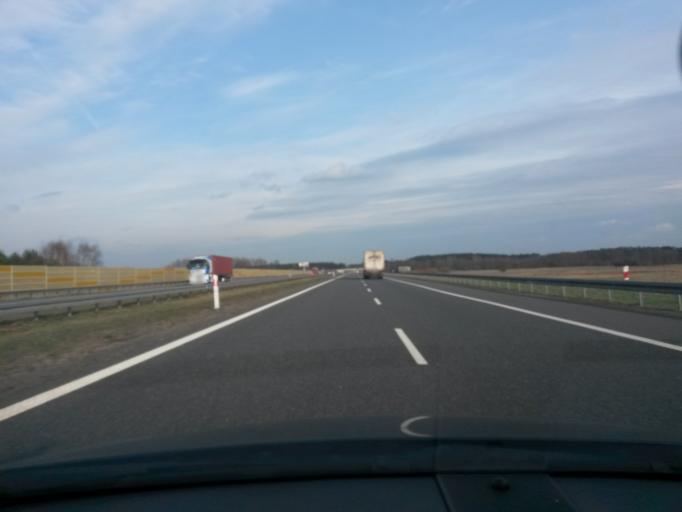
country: PL
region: Lodz Voivodeship
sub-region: Powiat zgierski
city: Parzeczew
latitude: 51.9373
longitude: 19.2508
